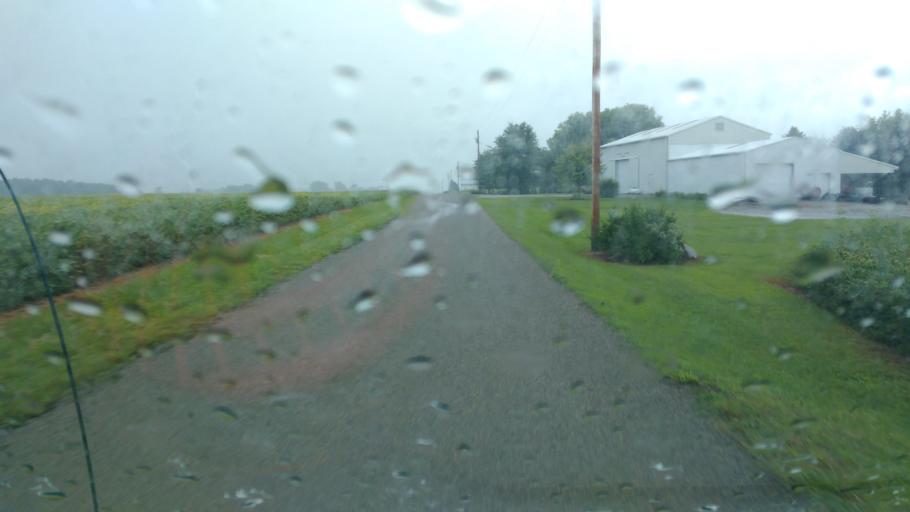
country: US
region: Ohio
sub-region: Hardin County
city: Kenton
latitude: 40.7056
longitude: -83.5967
